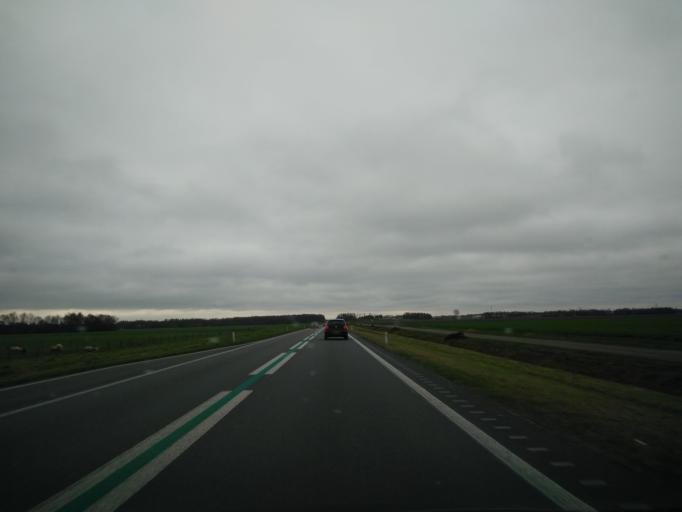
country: NL
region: Drenthe
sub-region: Gemeente Emmen
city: Emmer-Compascuum
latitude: 52.9004
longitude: 7.0383
